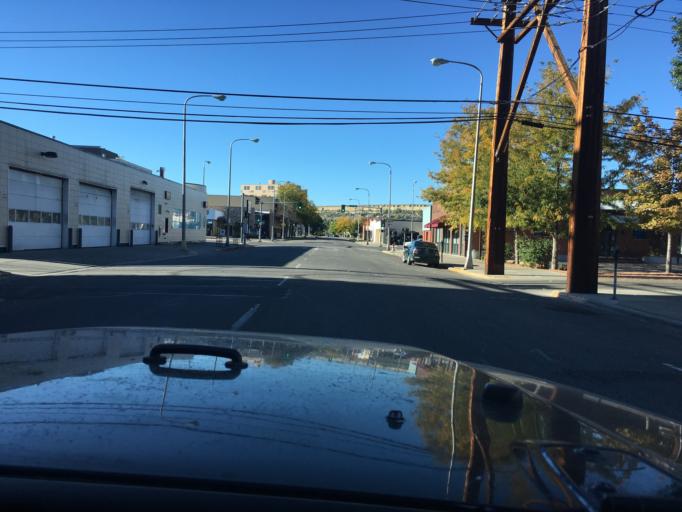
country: US
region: Montana
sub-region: Yellowstone County
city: Billings
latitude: 45.7833
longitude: -108.5015
